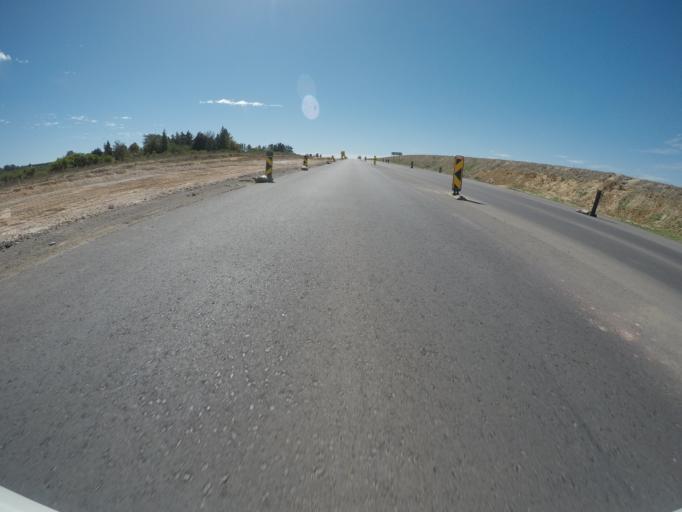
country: ZA
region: Western Cape
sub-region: West Coast District Municipality
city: Malmesbury
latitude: -33.5045
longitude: 18.6617
